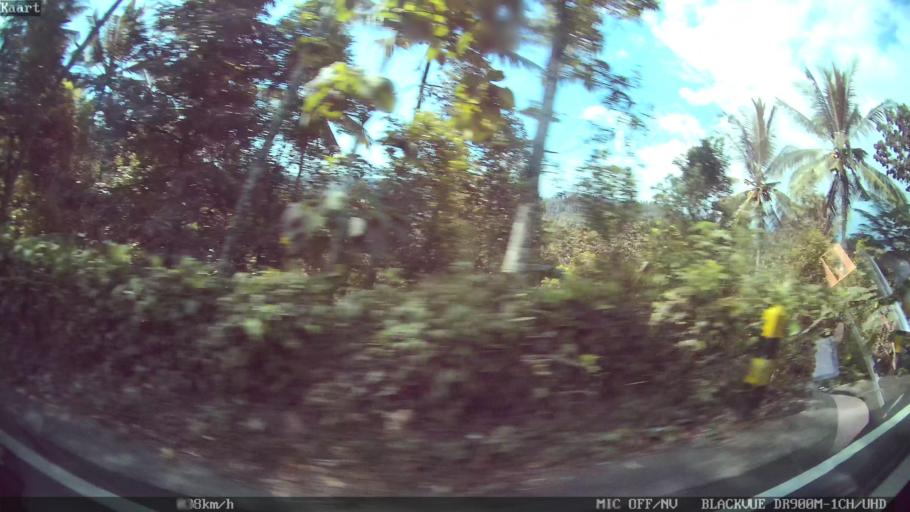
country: ID
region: Bali
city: Subuk
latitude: -8.2892
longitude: 114.9777
